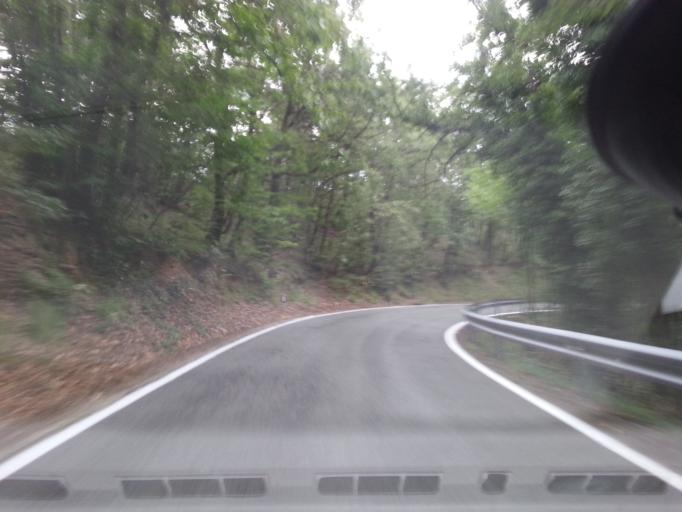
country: IT
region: Piedmont
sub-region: Provincia di Torino
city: Valgioie
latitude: 45.0667
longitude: 7.3711
